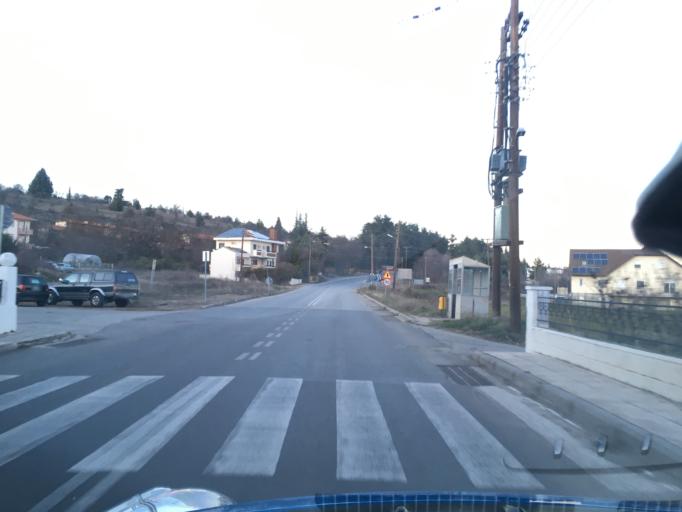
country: GR
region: West Macedonia
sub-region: Nomos Kozanis
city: Kozani
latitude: 40.2731
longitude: 21.7816
